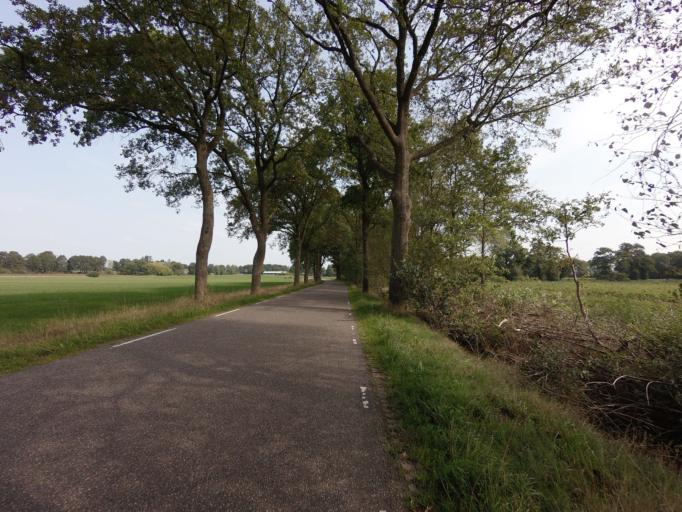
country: NL
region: Drenthe
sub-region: Gemeente Assen
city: Assen
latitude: 52.9619
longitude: 6.6129
